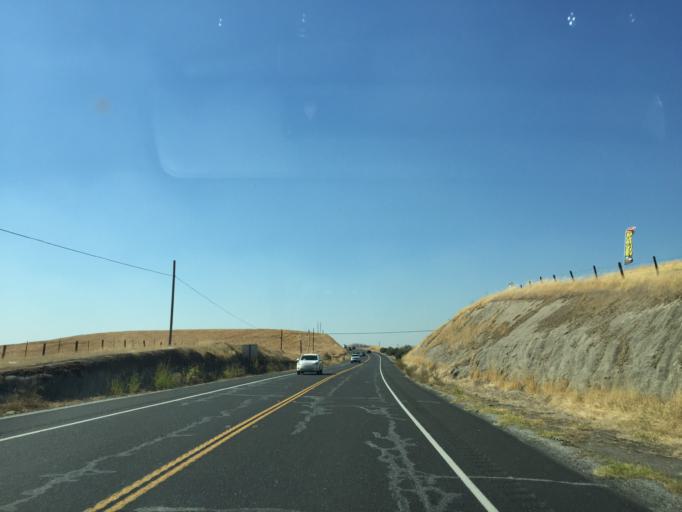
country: US
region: California
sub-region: Stanislaus County
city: East Oakdale
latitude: 37.8144
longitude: -120.6573
